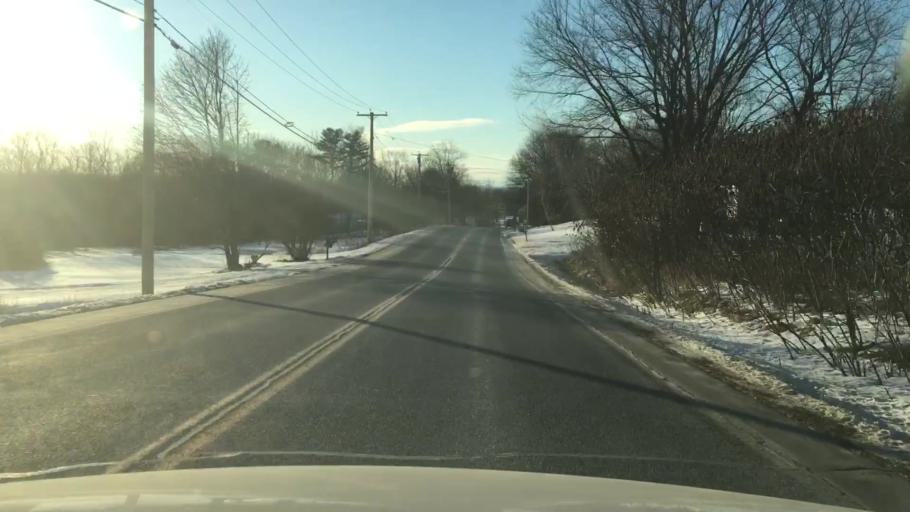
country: US
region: Maine
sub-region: Penobscot County
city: Eddington
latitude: 44.8300
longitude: -68.6675
